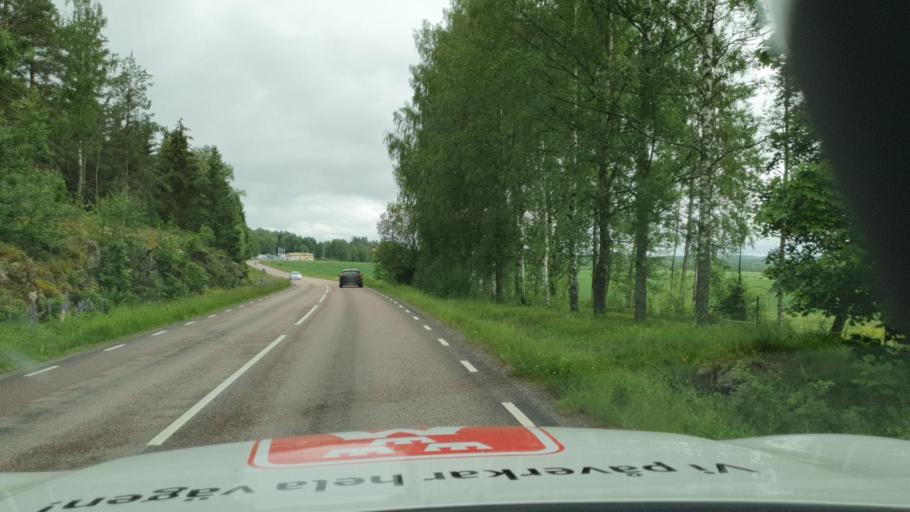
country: SE
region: Vaermland
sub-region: Karlstads Kommun
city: Edsvalla
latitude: 59.4219
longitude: 13.2066
